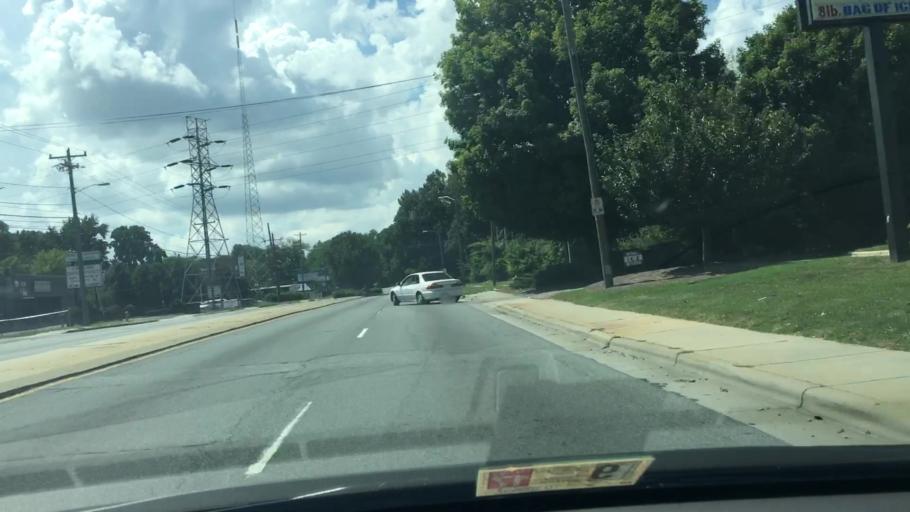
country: US
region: North Carolina
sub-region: Mecklenburg County
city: Charlotte
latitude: 35.2547
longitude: -80.8019
